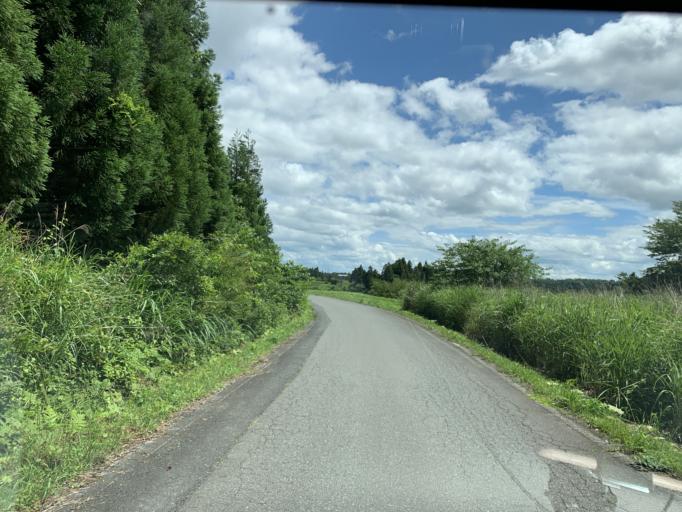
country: JP
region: Iwate
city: Ichinoseki
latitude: 38.9293
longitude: 141.0422
